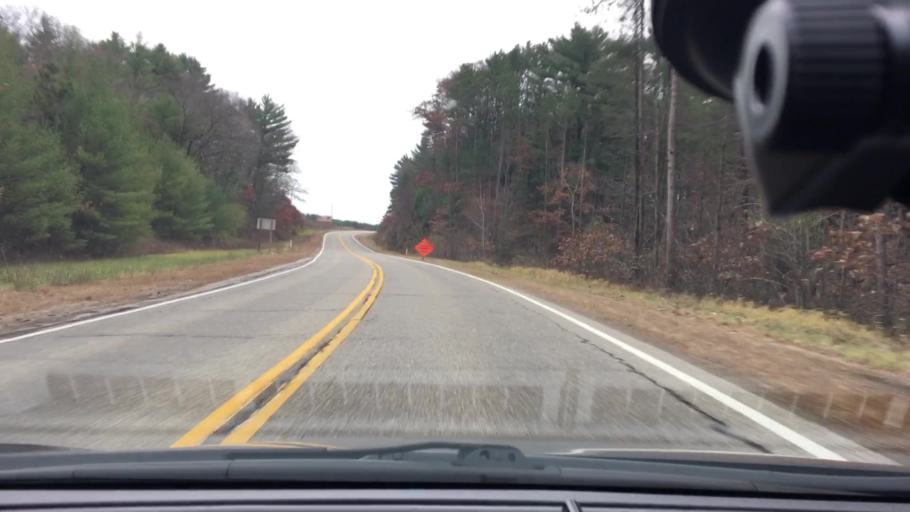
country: US
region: Wisconsin
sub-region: Columbia County
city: Wisconsin Dells
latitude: 43.6403
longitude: -89.8008
